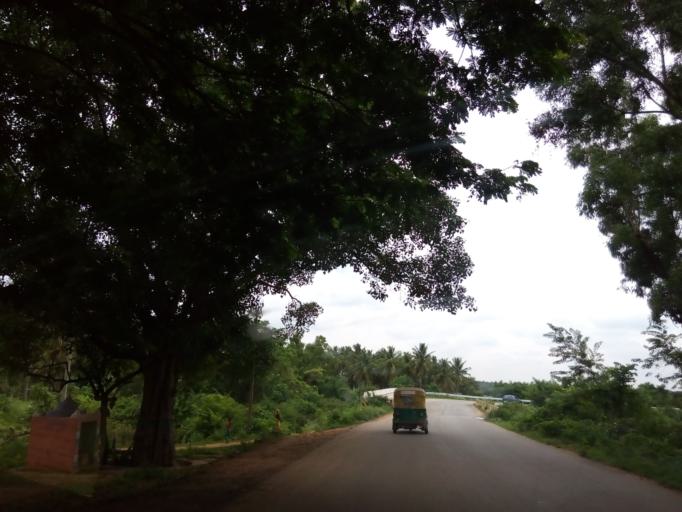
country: IN
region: Karnataka
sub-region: Hassan
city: Channarayapatna
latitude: 12.8776
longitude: 76.4251
